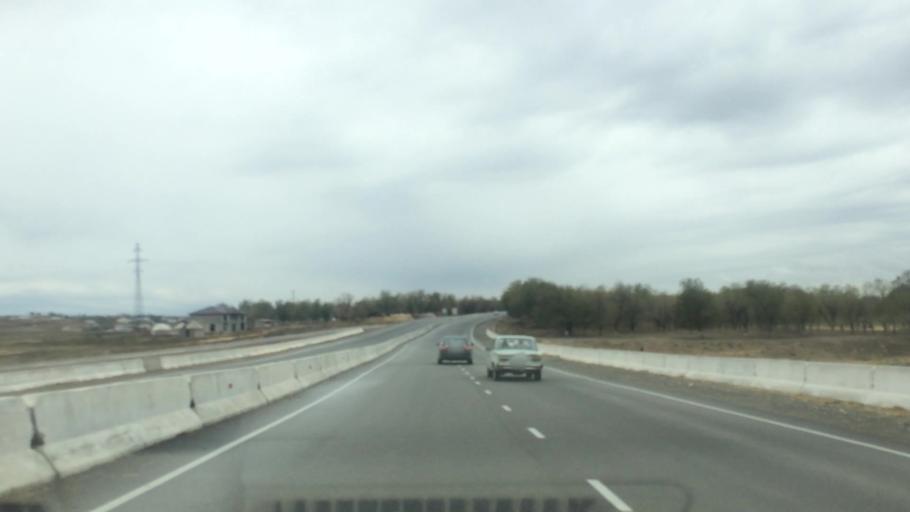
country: UZ
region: Samarqand
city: Bulung'ur
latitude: 39.9205
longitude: 67.5160
